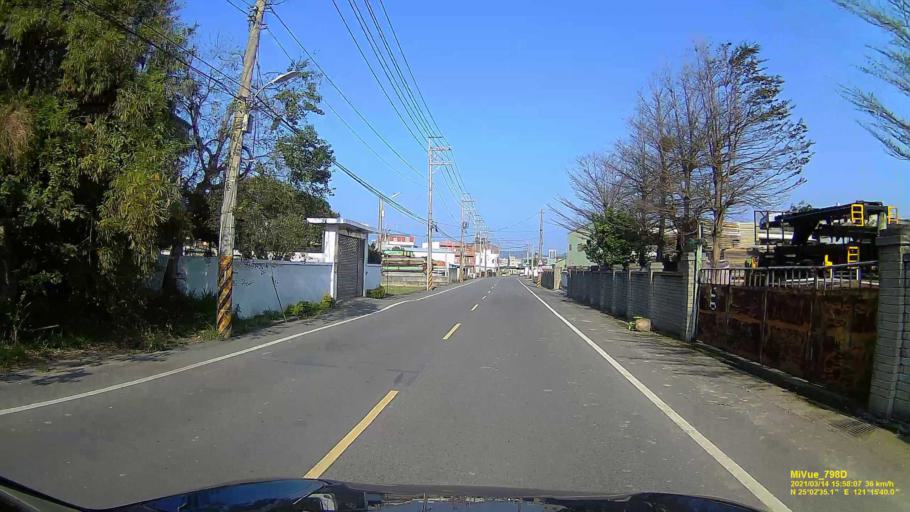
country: TW
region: Taiwan
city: Taoyuan City
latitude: 25.0432
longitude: 121.2614
